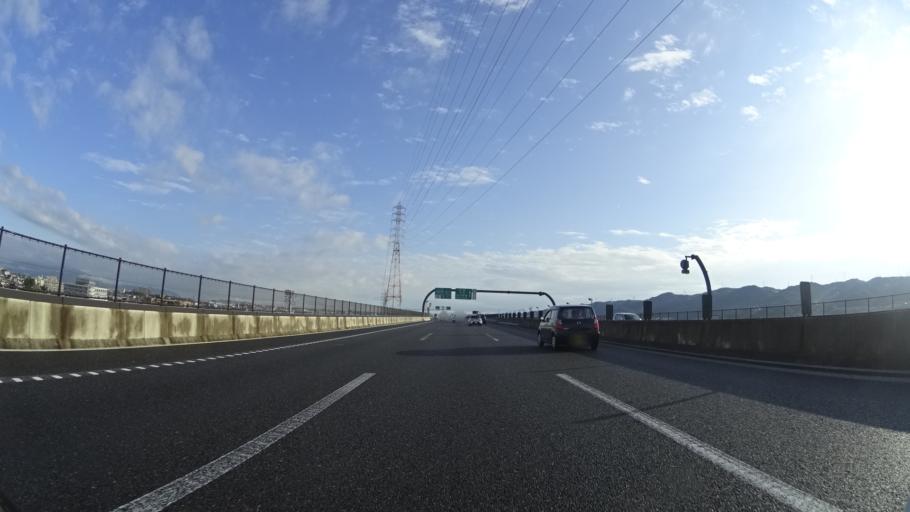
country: JP
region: Osaka
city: Neyagawa
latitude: 34.7741
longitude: 135.6630
